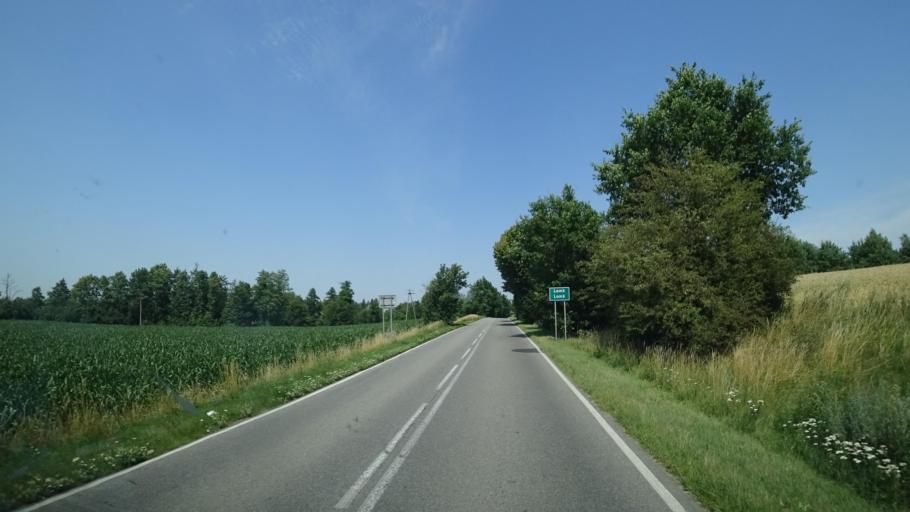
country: PL
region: Pomeranian Voivodeship
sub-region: Powiat koscierski
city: Dziemiany
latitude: 53.9551
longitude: 17.7454
